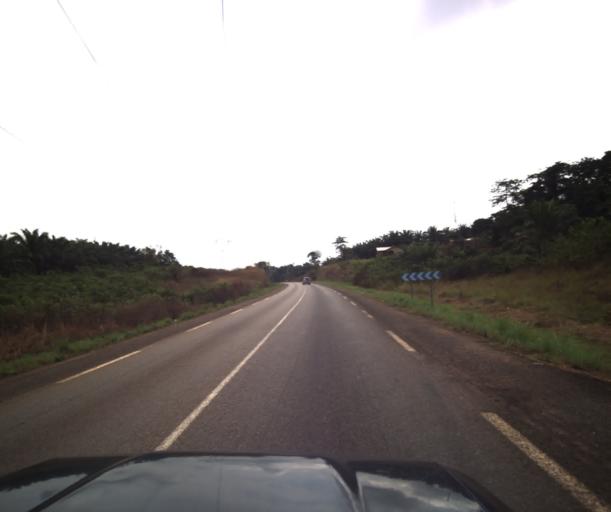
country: CM
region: Littoral
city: Edea
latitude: 3.8358
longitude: 10.4441
